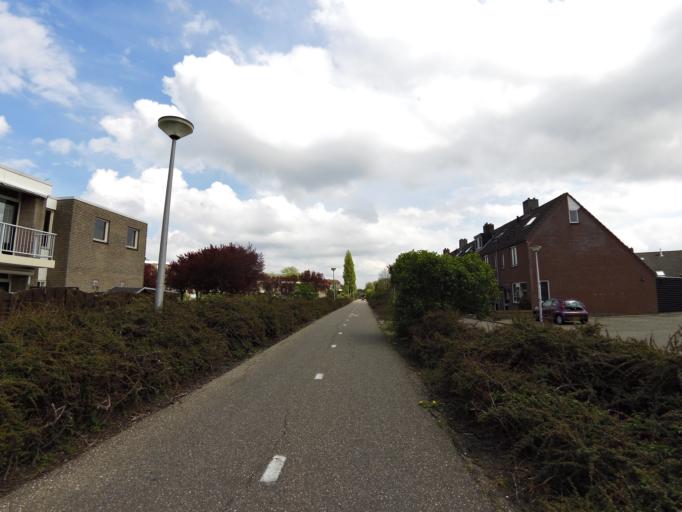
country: NL
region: South Holland
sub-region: Gemeente Hellevoetsluis
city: Hellevoetsluis
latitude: 51.8338
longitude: 4.1550
